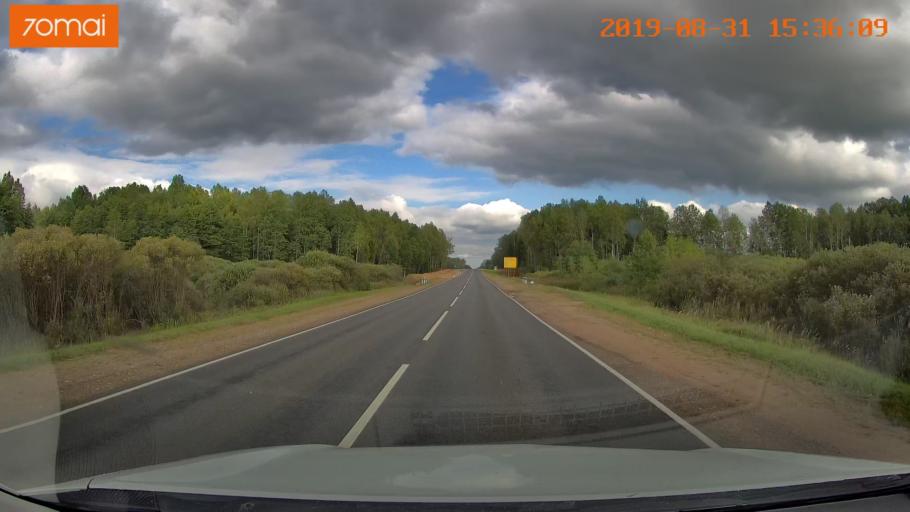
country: RU
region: Kaluga
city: Mosal'sk
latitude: 54.6093
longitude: 34.7518
